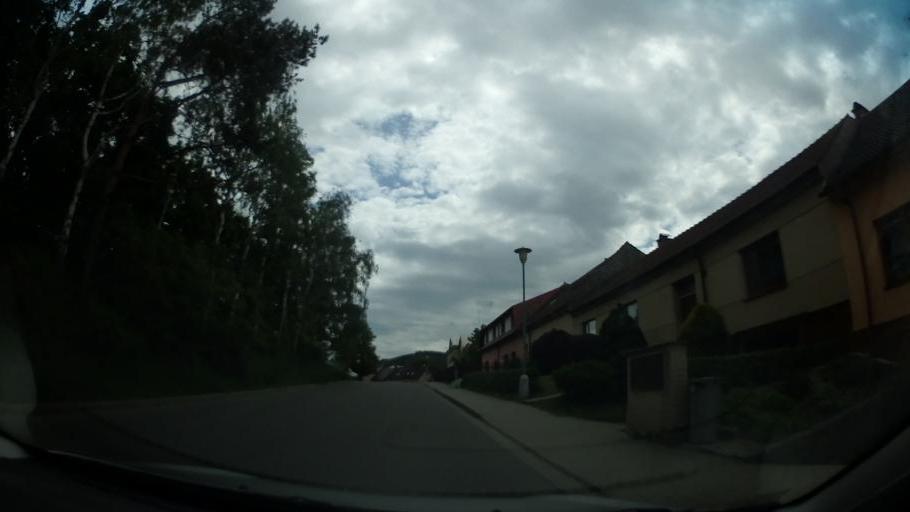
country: CZ
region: Pardubicky
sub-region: Okres Svitavy
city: Moravska Trebova
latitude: 49.7619
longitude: 16.6524
